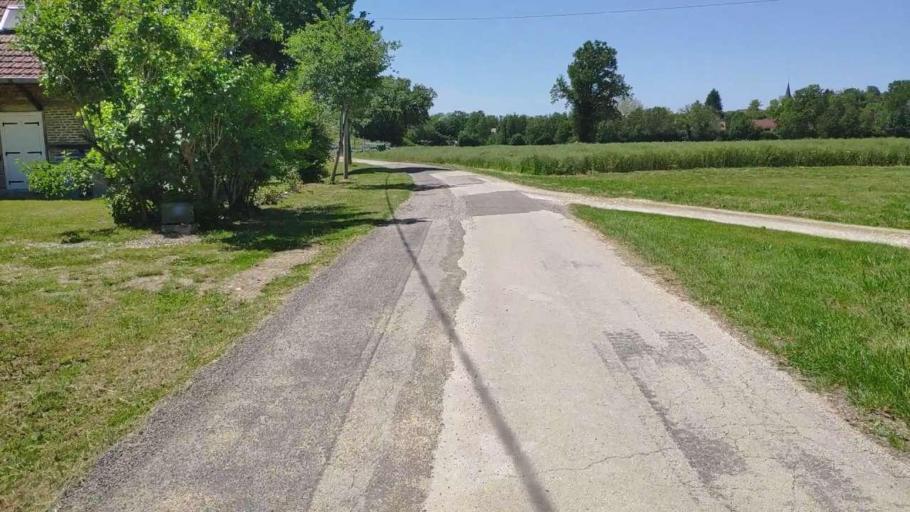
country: FR
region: Franche-Comte
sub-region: Departement du Jura
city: Bletterans
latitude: 46.7454
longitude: 5.4087
